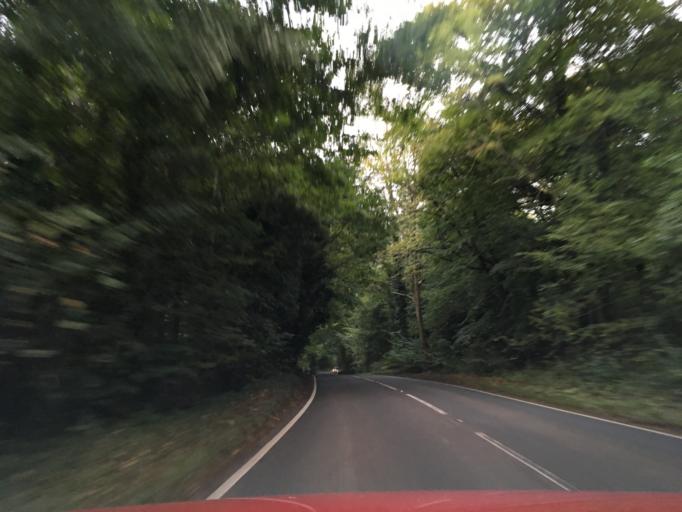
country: GB
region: England
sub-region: Gloucestershire
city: Stonehouse
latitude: 51.7185
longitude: -2.2615
